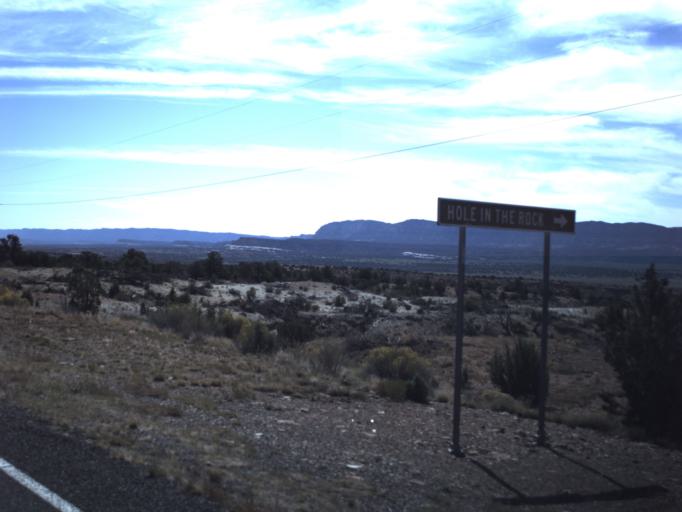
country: US
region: Utah
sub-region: Wayne County
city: Loa
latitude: 37.7287
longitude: -111.5336
